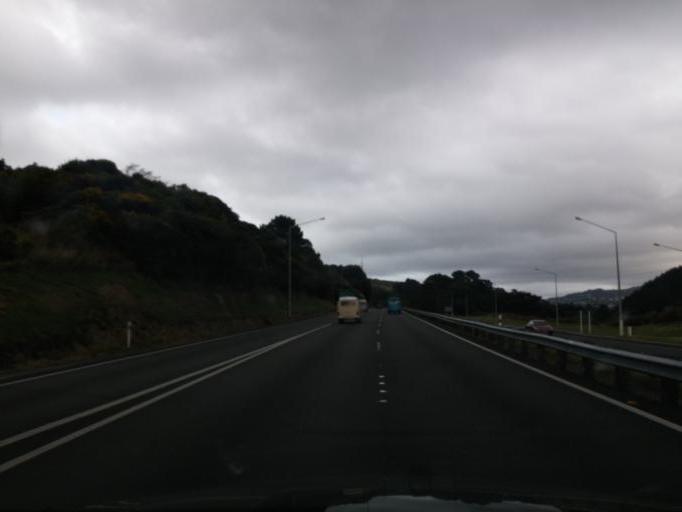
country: NZ
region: Wellington
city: Petone
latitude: -41.1873
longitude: 174.8320
